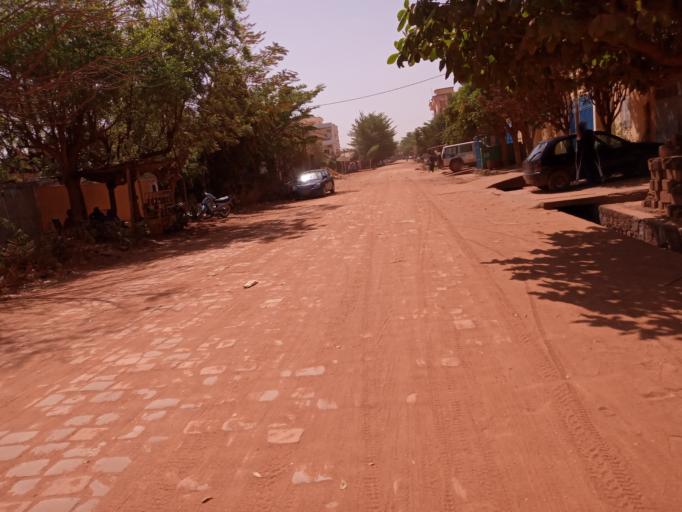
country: ML
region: Bamako
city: Bamako
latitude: 12.5860
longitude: -7.9557
